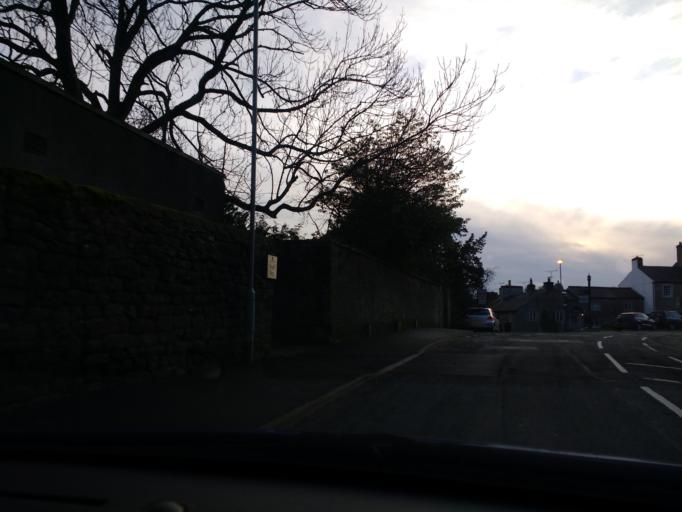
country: GB
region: England
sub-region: North Yorkshire
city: Settle
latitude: 54.0724
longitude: -2.2865
